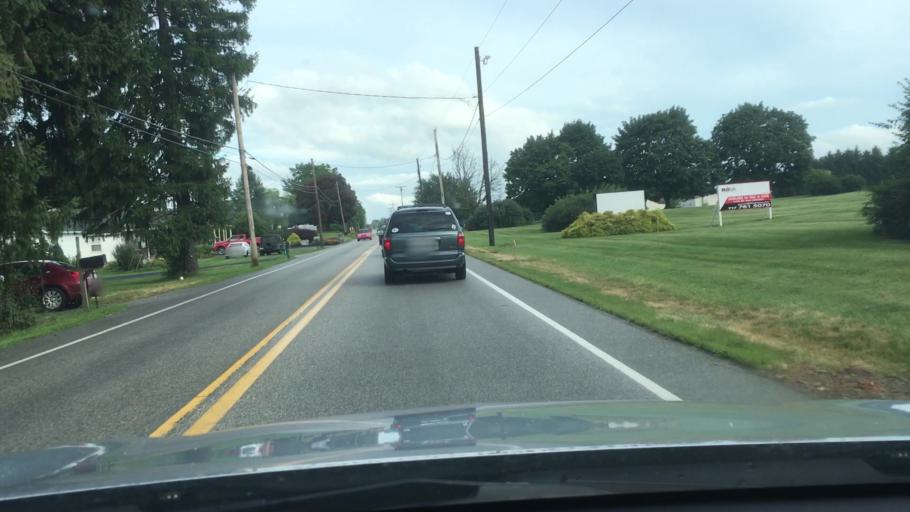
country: US
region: Pennsylvania
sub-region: Cumberland County
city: Carlisle
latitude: 40.1904
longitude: -77.1579
